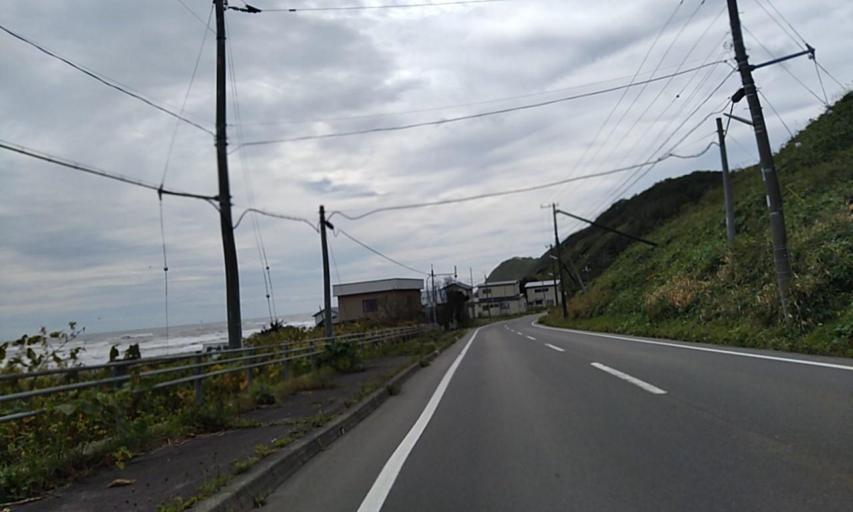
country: JP
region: Hokkaido
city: Kushiro
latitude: 42.8002
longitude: 143.8116
